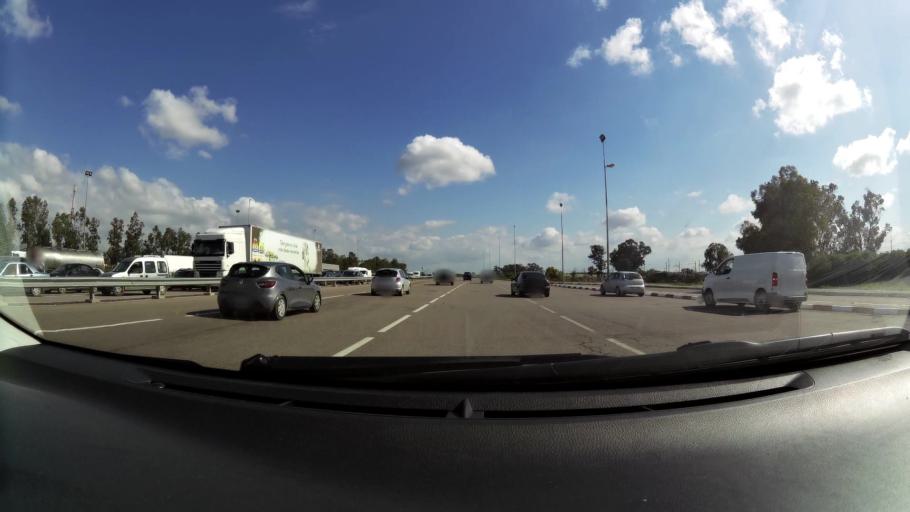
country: MA
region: Chaouia-Ouardigha
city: Nouaseur
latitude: 33.3663
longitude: -7.6204
